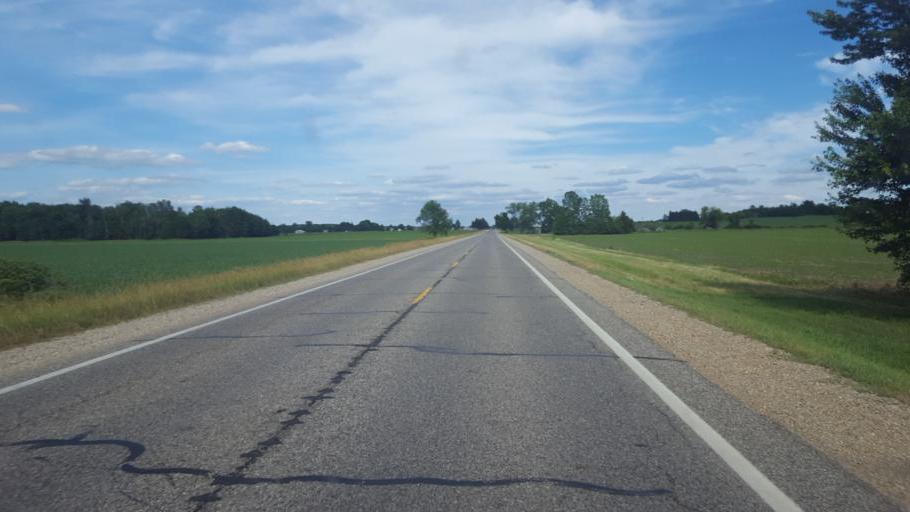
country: US
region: Michigan
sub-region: Eaton County
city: Charlotte
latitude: 42.5680
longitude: -84.9303
